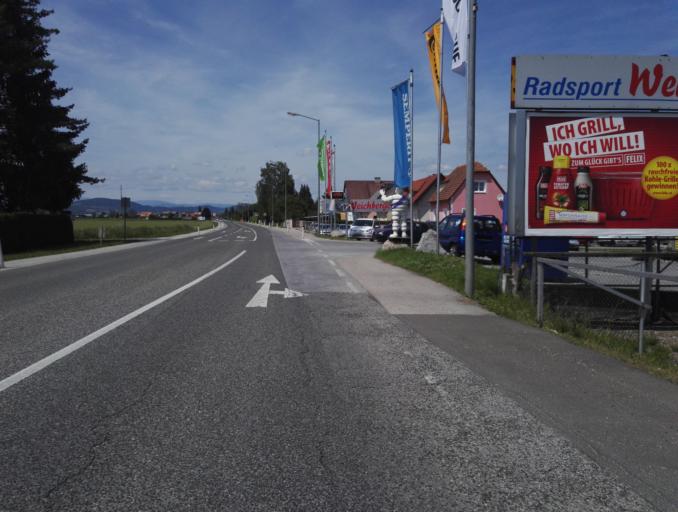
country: AT
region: Styria
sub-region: Politischer Bezirk Graz-Umgebung
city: Gossendorf
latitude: 46.9772
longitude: 15.4688
